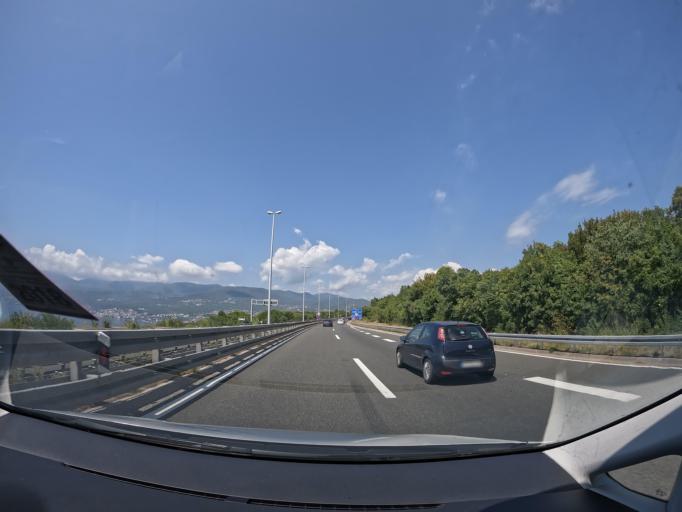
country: HR
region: Primorsko-Goranska
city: Rubesi
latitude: 45.3493
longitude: 14.3654
